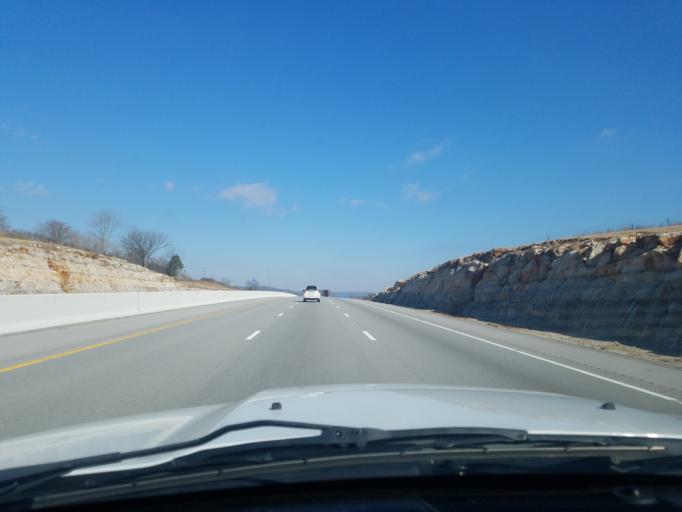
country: US
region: Kentucky
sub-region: Hart County
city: Horse Cave
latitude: 37.2269
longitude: -85.9316
